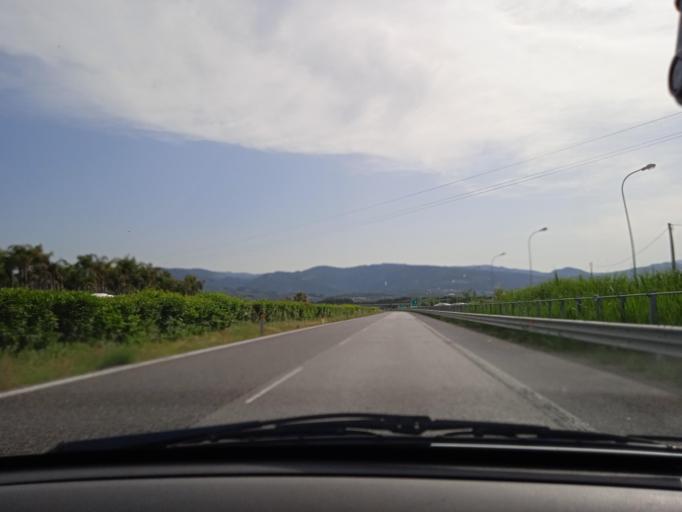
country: IT
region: Sicily
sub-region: Messina
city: Tonnarella
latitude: 38.1240
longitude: 15.1216
